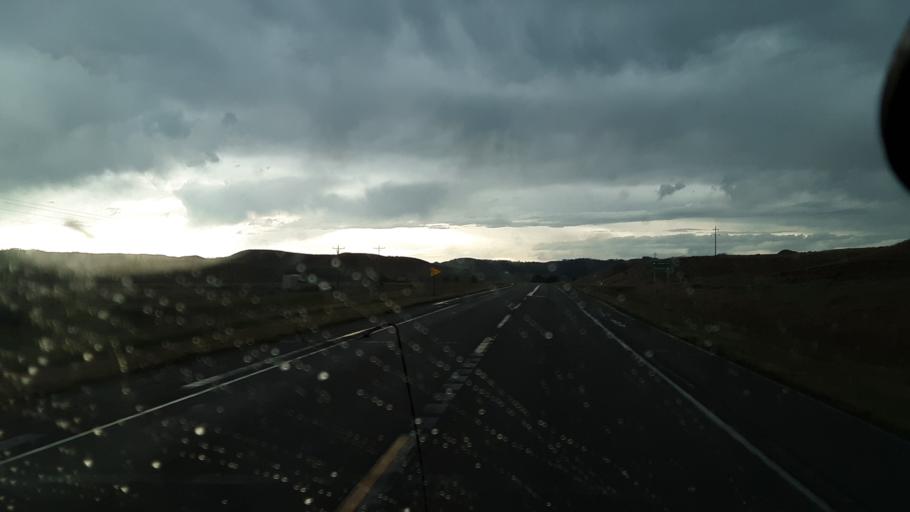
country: US
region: Montana
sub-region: Powder River County
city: Broadus
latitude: 45.5406
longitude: -105.8241
